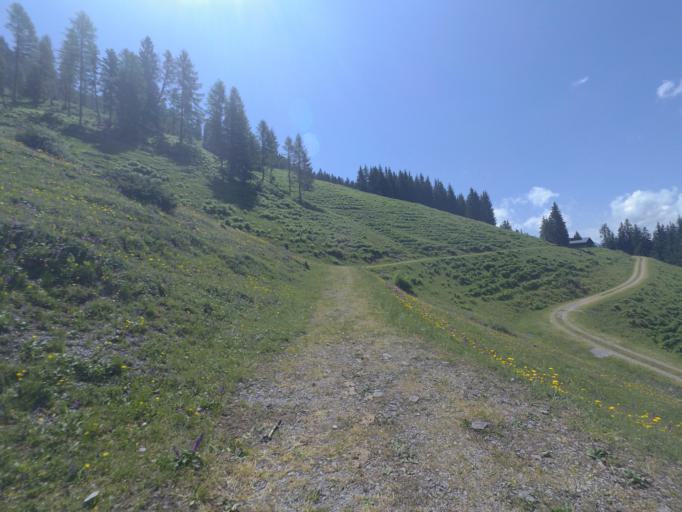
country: AT
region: Salzburg
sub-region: Politischer Bezirk Zell am See
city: Dienten am Hochkonig
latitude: 47.4181
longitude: 13.0025
